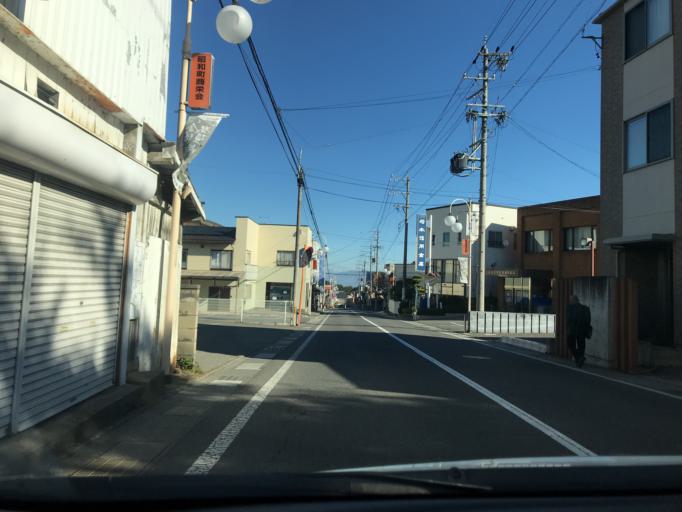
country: JP
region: Nagano
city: Toyoshina
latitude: 36.1969
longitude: 137.8550
